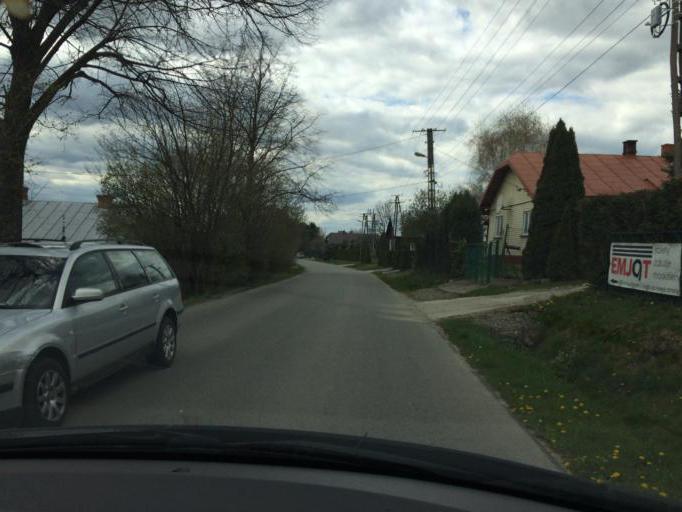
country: PL
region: Subcarpathian Voivodeship
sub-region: Powiat krosnienski
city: Chorkowka
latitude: 49.6077
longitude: 21.6426
